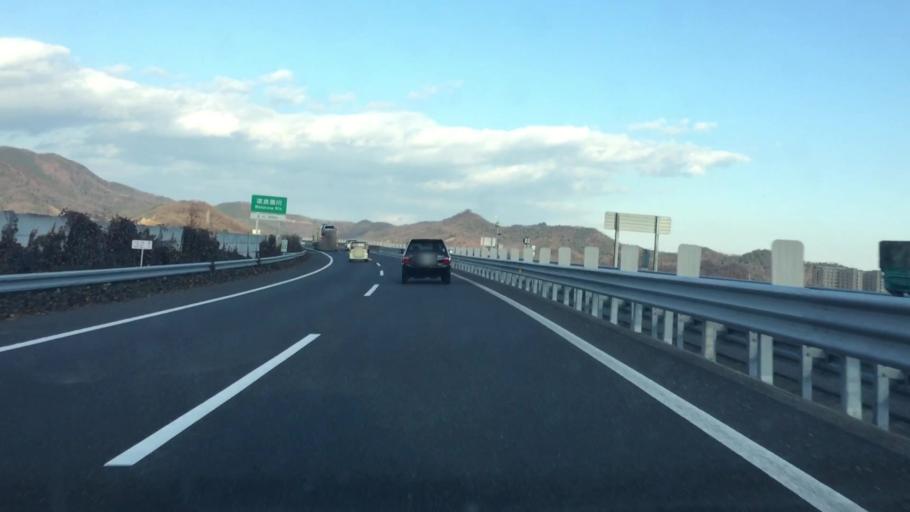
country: JP
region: Tochigi
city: Ashikaga
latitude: 36.3380
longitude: 139.4073
